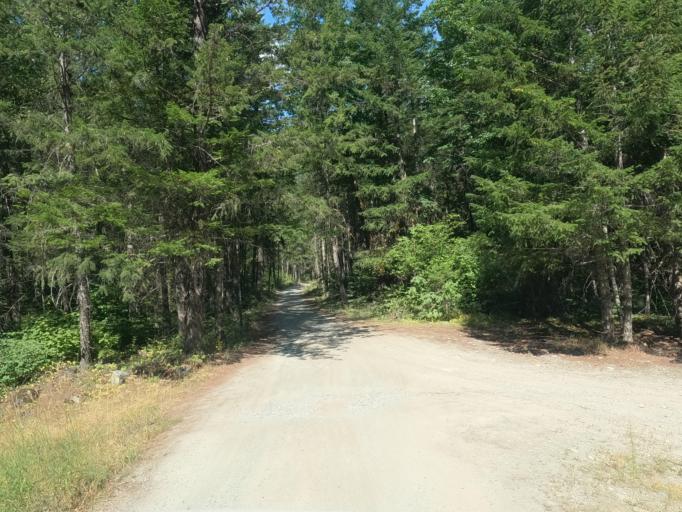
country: CA
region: British Columbia
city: Pemberton
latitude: 50.3515
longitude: -122.7299
